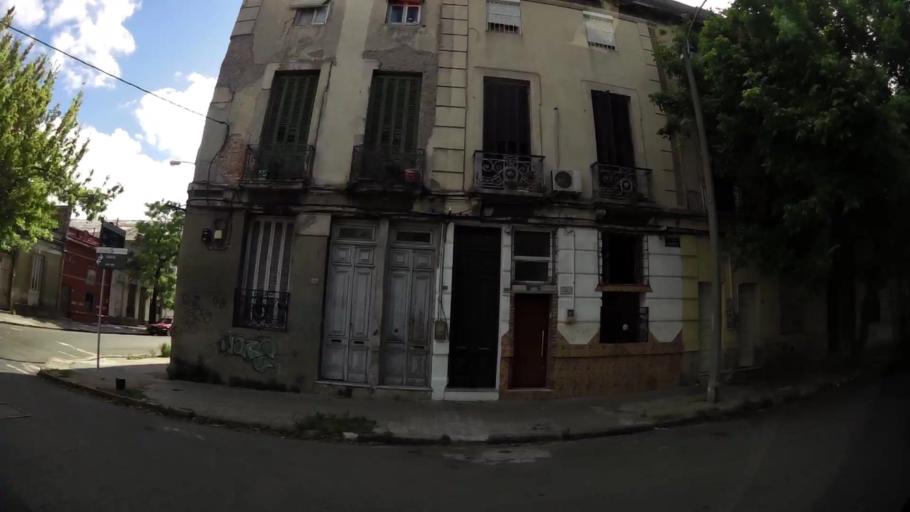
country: UY
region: Montevideo
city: Montevideo
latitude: -34.8949
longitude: -56.1784
